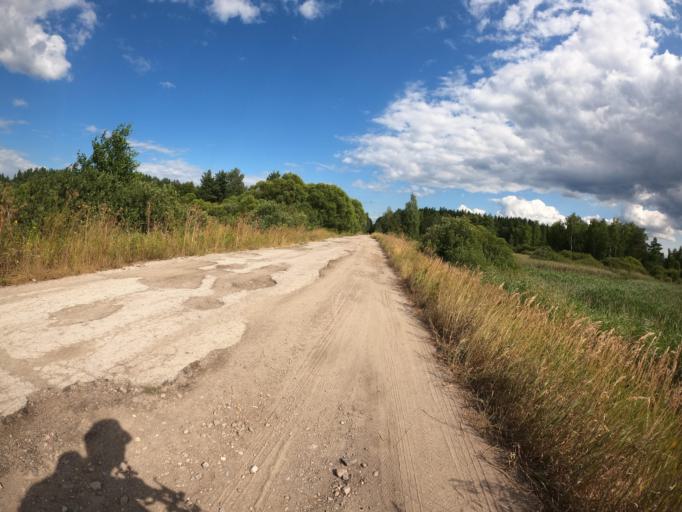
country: RU
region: Moskovskaya
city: Konobeyevo
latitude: 55.3855
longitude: 38.6983
